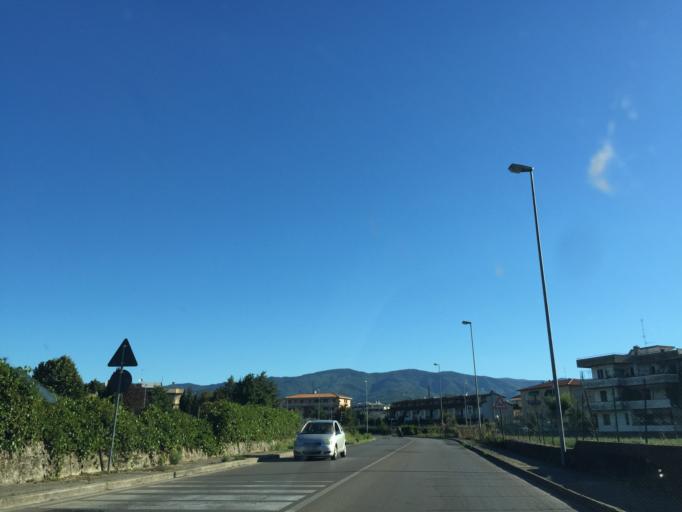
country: IT
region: Tuscany
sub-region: Provincia di Pistoia
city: Pistoia
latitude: 43.9338
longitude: 10.8968
